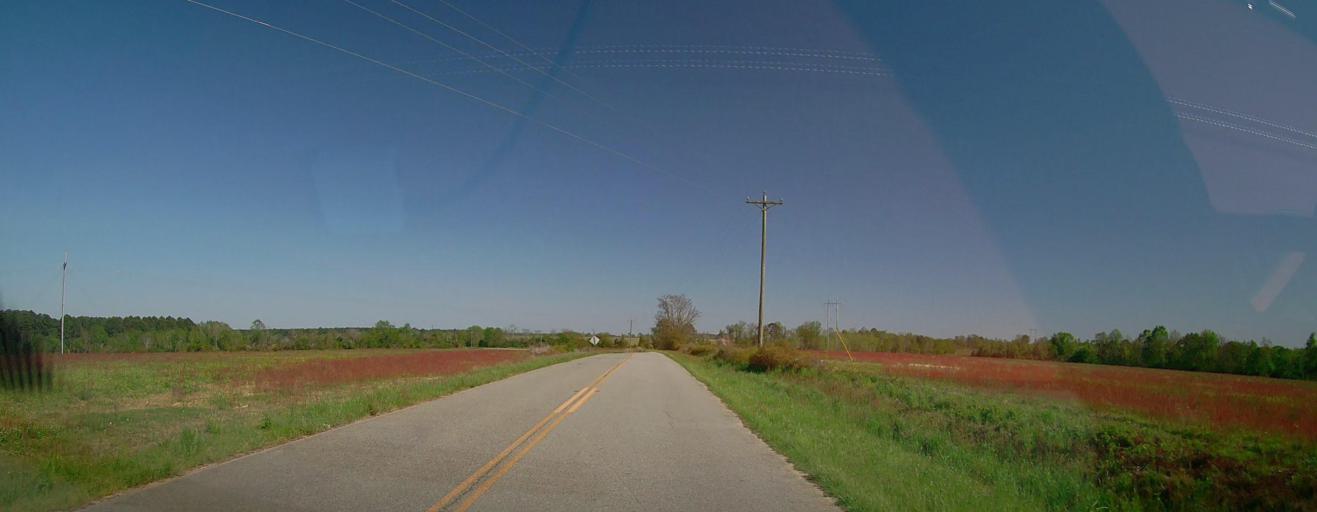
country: US
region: Georgia
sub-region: Pulaski County
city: Hawkinsville
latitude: 32.2482
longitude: -83.5825
